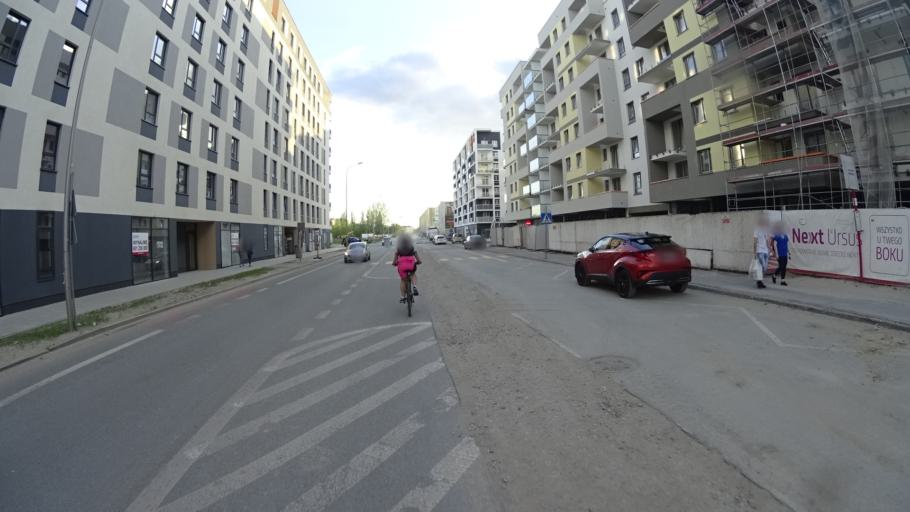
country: PL
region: Masovian Voivodeship
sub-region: Warszawa
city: Ursus
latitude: 52.2042
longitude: 20.8799
